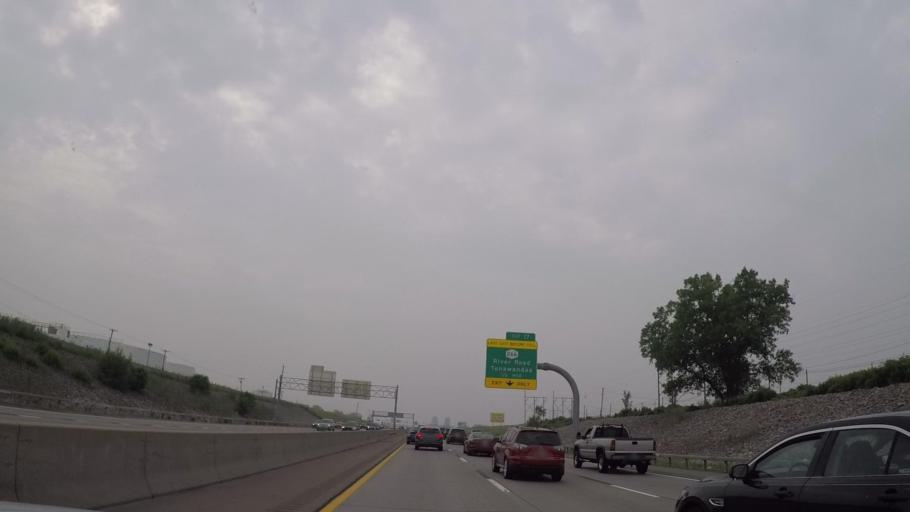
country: US
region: New York
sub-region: Erie County
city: Grandyle Village
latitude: 42.9899
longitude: -78.9197
